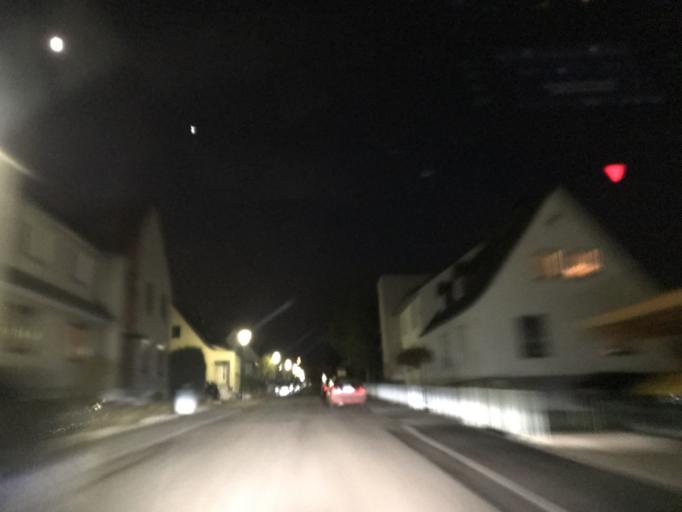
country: DE
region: Hesse
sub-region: Regierungsbezirk Kassel
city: Fuldabruck
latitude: 51.3018
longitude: 9.4523
